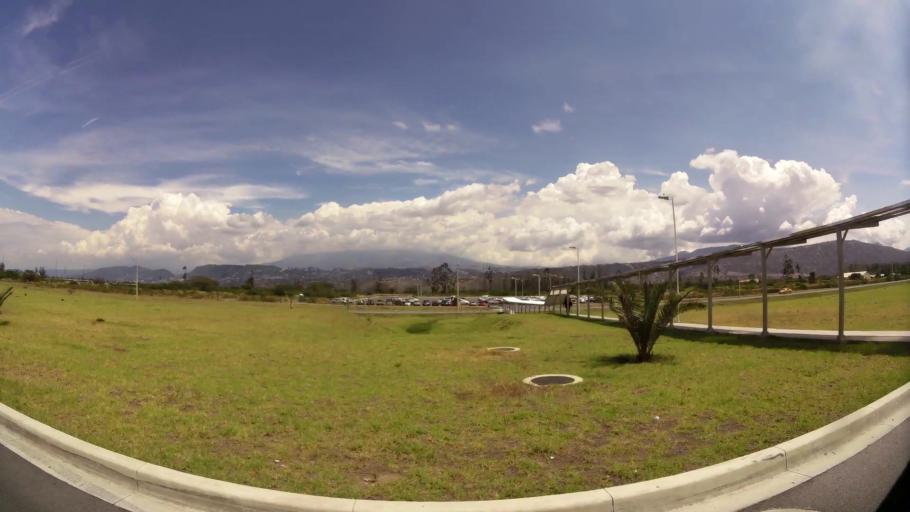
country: EC
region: Pichincha
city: Quito
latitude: -0.1263
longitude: -78.3629
